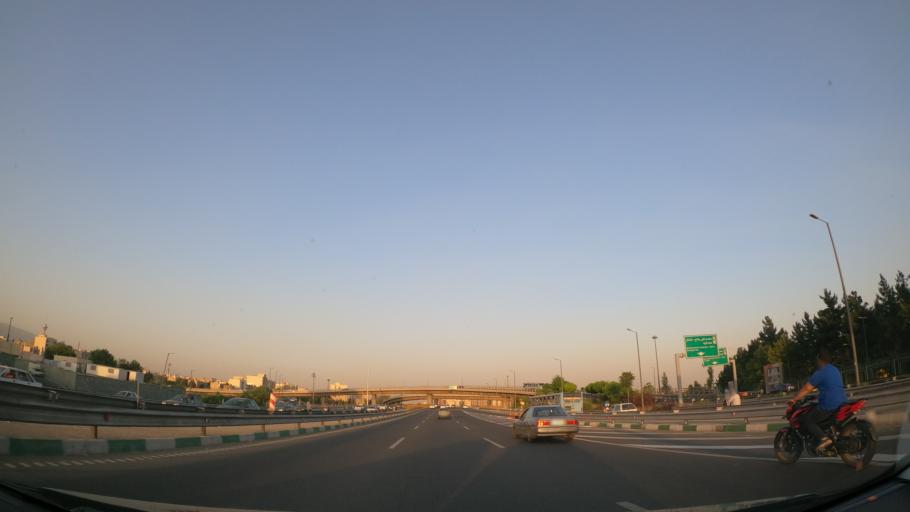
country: IR
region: Tehran
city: Tehran
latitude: 35.7128
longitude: 51.3336
